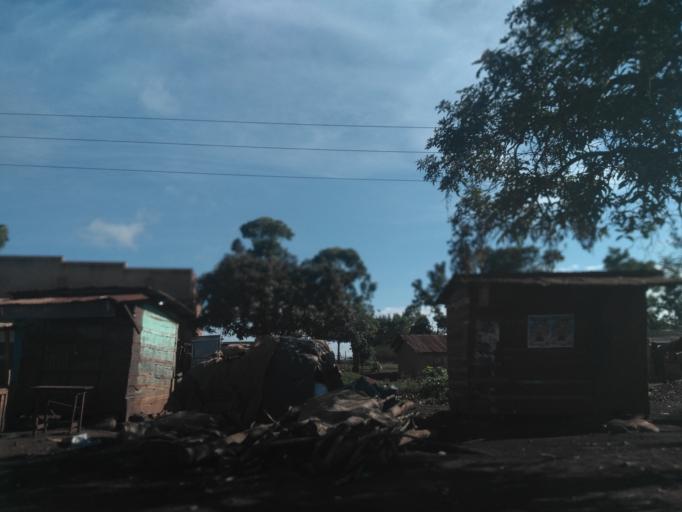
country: UG
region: Eastern Region
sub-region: Jinja District
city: Jinja
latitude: 0.4538
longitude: 33.1887
